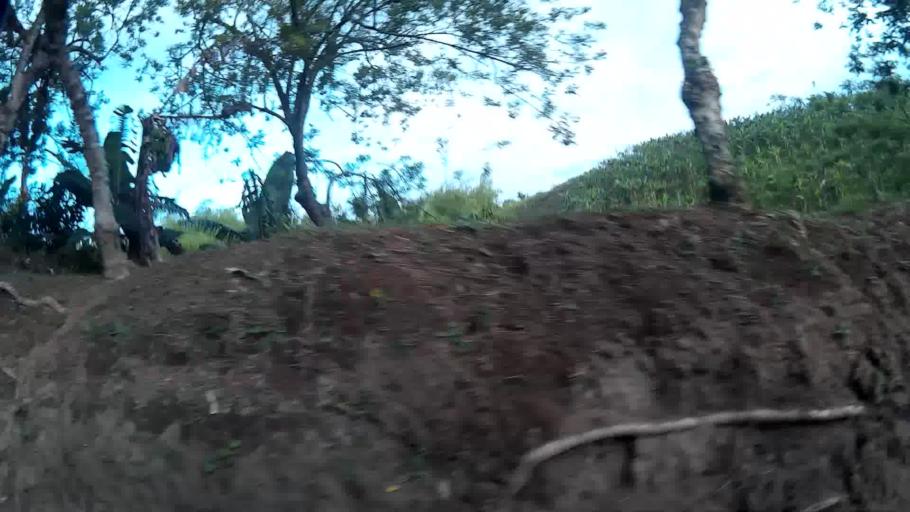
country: CO
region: Valle del Cauca
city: Ulloa
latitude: 4.7366
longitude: -75.7407
